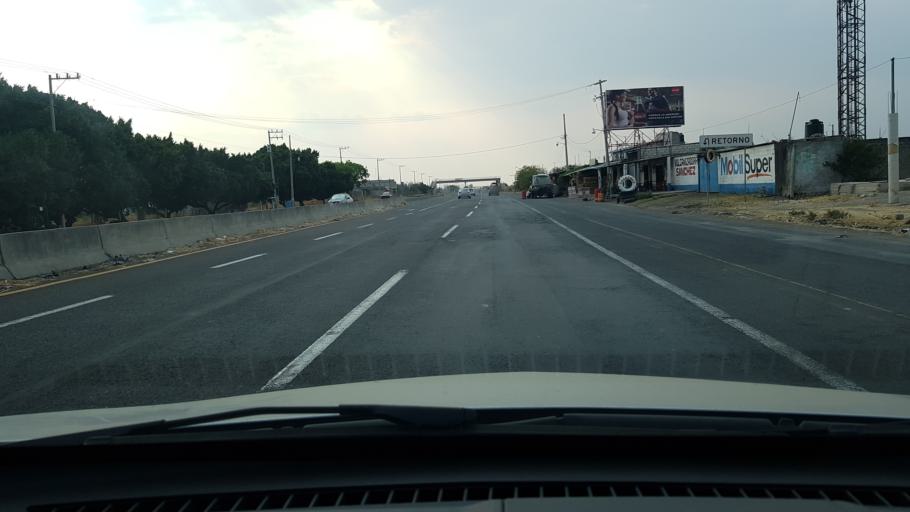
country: MX
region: Morelos
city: Amayuca
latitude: 18.7368
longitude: -98.8234
